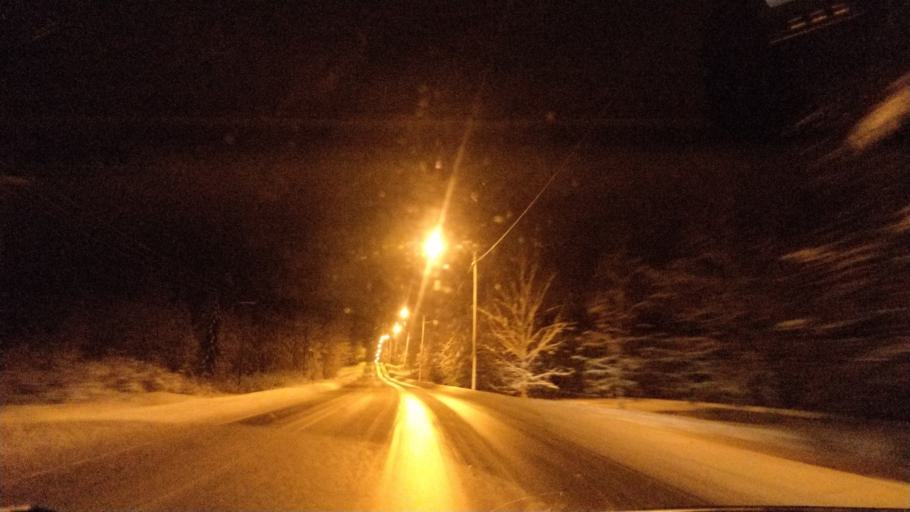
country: FI
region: Lapland
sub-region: Rovaniemi
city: Rovaniemi
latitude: 66.3014
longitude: 25.3540
